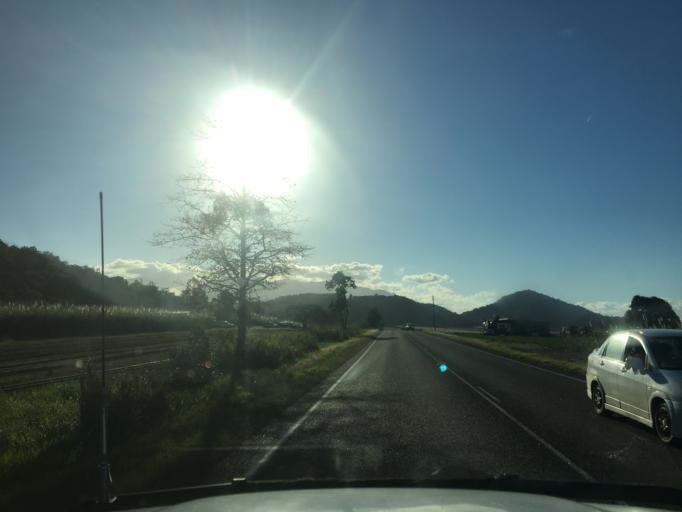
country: AU
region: Queensland
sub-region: Cairns
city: Port Douglas
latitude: -16.4816
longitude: 145.4088
